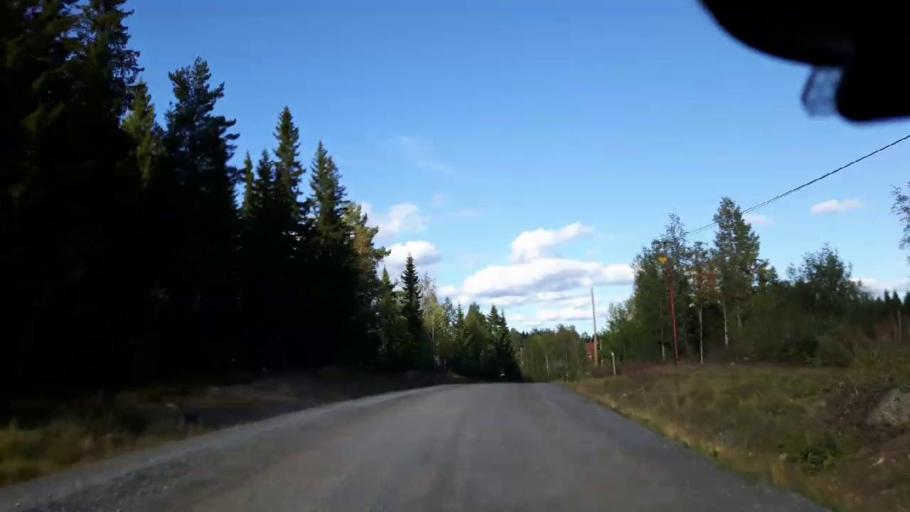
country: SE
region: Jaemtland
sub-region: Ragunda Kommun
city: Hammarstrand
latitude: 63.4322
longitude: 16.1808
